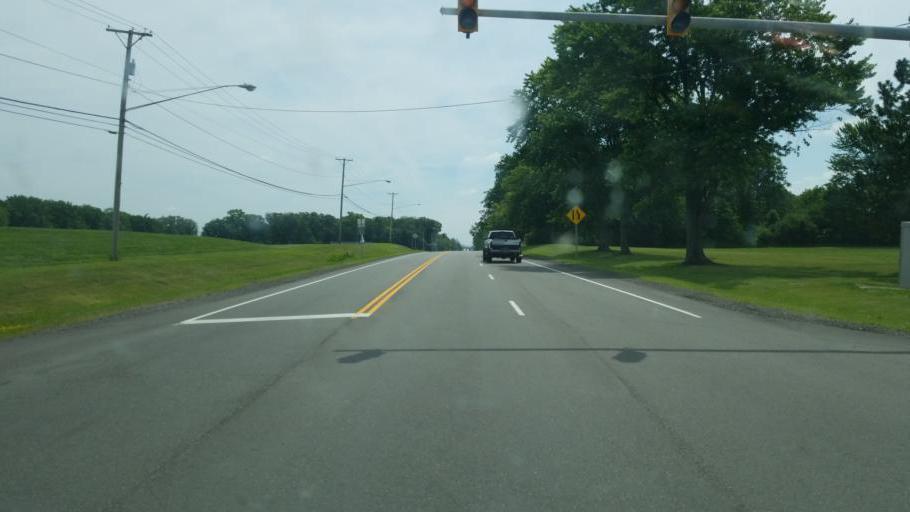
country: US
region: Ohio
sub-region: Summit County
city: Macedonia
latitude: 41.3114
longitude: -81.4820
